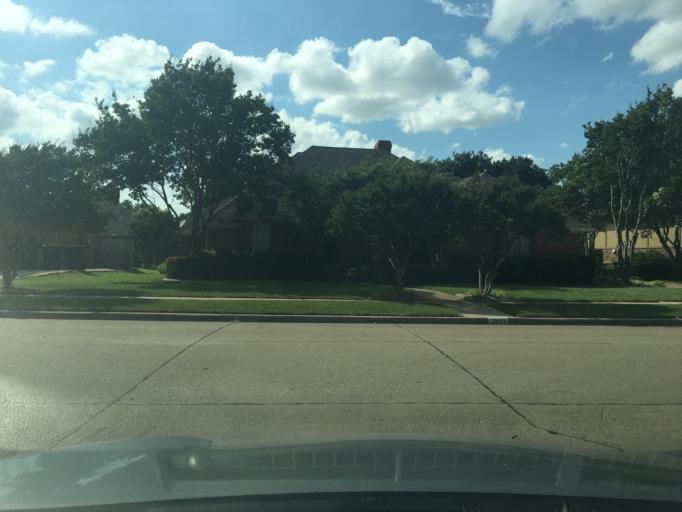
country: US
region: Texas
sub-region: Dallas County
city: Garland
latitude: 32.9359
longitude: -96.6756
